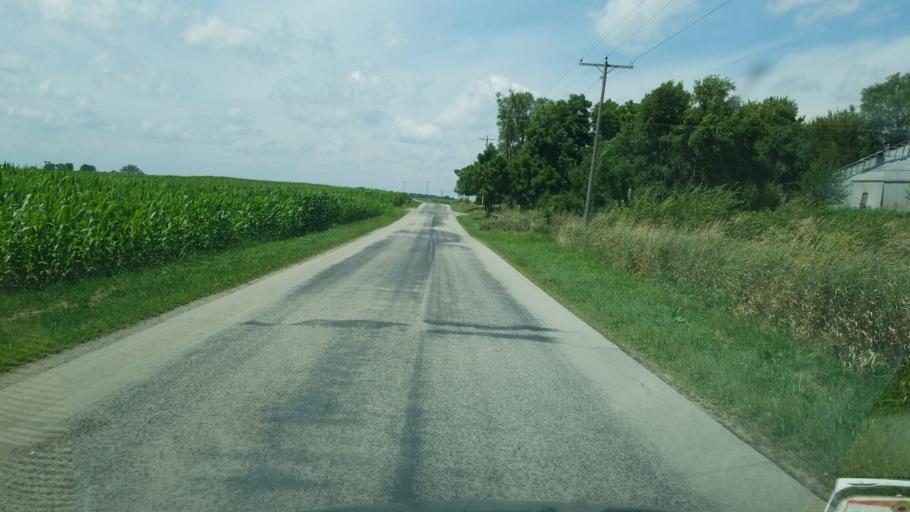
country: US
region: Ohio
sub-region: Hardin County
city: Forest
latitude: 40.8685
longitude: -83.4917
